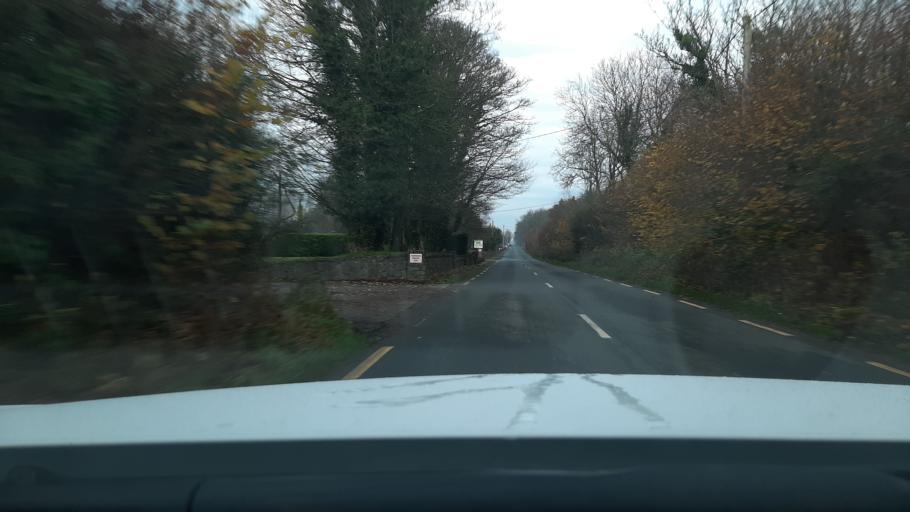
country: IE
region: Leinster
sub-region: Kildare
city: Rathangan
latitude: 53.2370
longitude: -7.0104
